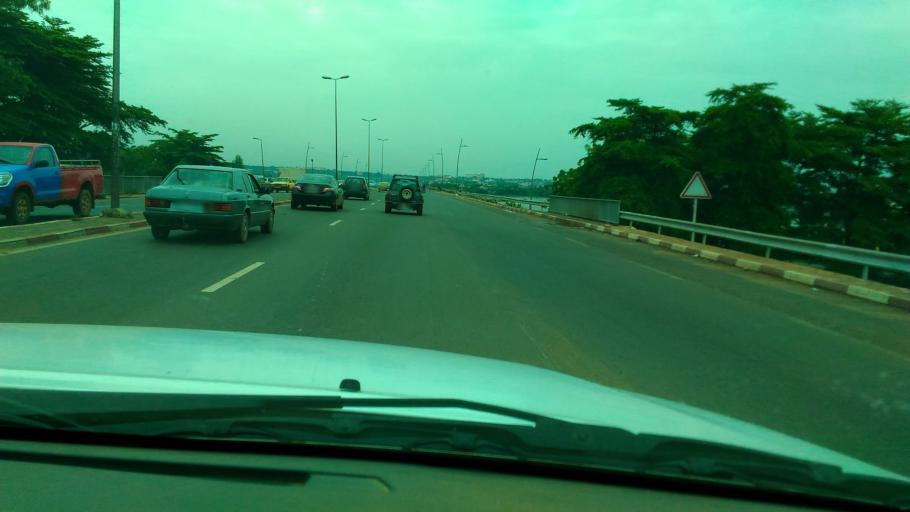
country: ML
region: Bamako
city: Bamako
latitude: 12.6282
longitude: -8.0082
